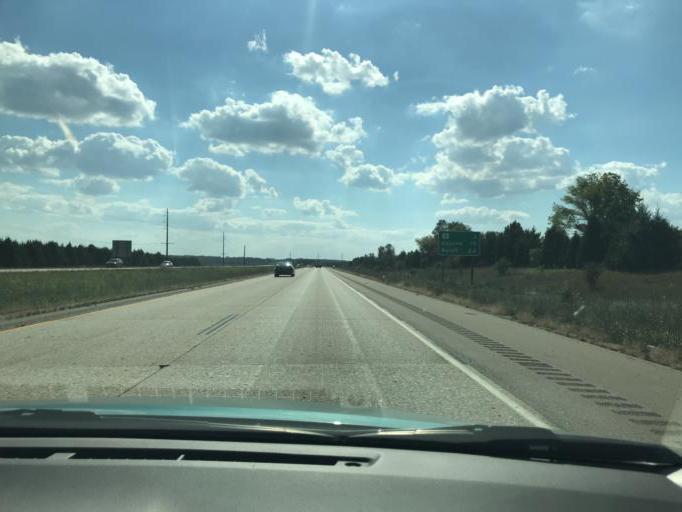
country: US
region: Wisconsin
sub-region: Walworth County
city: Delavan
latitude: 42.6182
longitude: -88.6321
